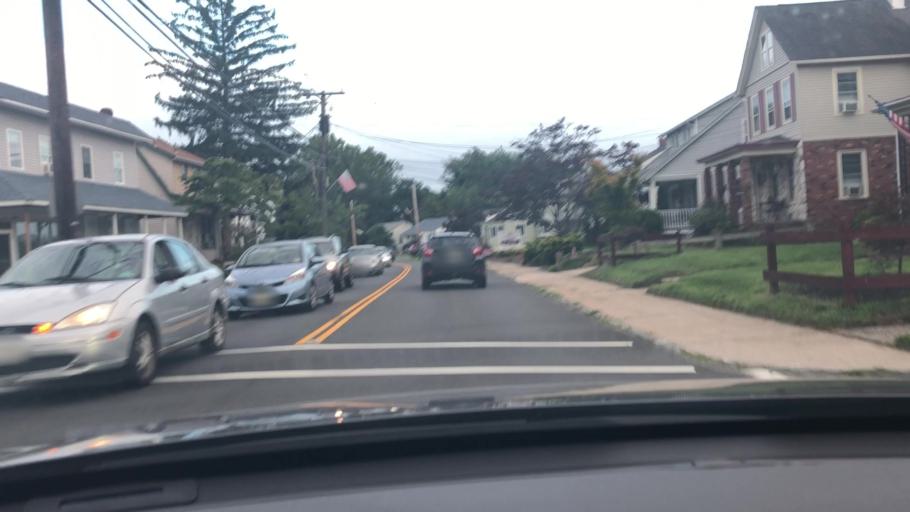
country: US
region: New Jersey
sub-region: Middlesex County
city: Milltown
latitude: 40.4450
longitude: -74.4333
